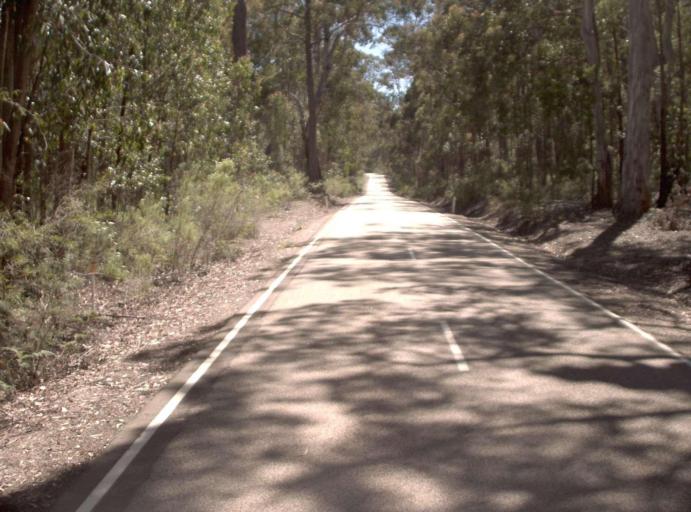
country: AU
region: Victoria
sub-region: East Gippsland
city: Lakes Entrance
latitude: -37.2950
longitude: 148.2527
